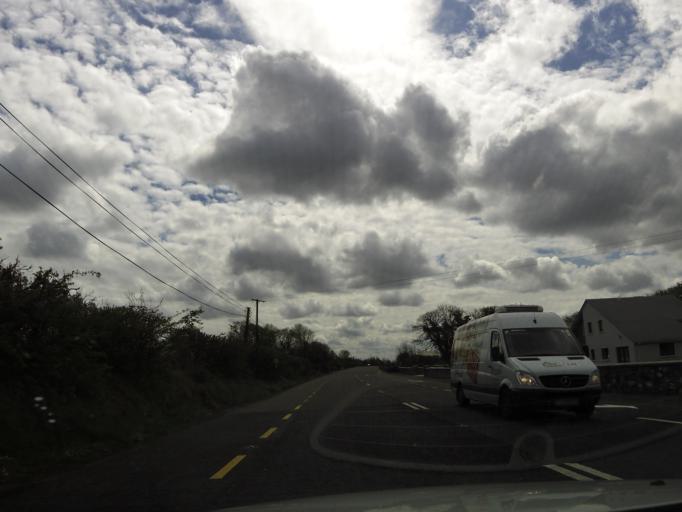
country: IE
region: Connaught
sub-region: County Galway
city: Tuam
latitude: 53.5563
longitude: -8.8423
